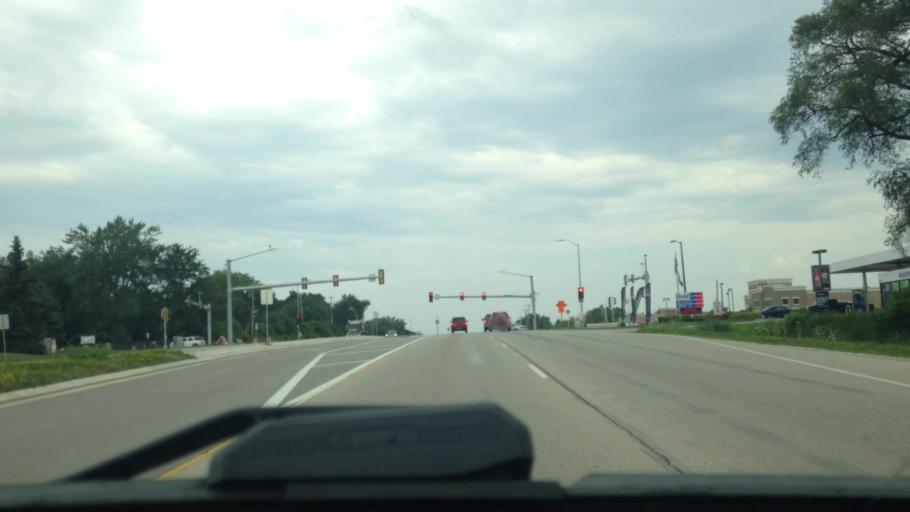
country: US
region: Wisconsin
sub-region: Waukesha County
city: Butler
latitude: 43.1192
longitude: -88.0838
